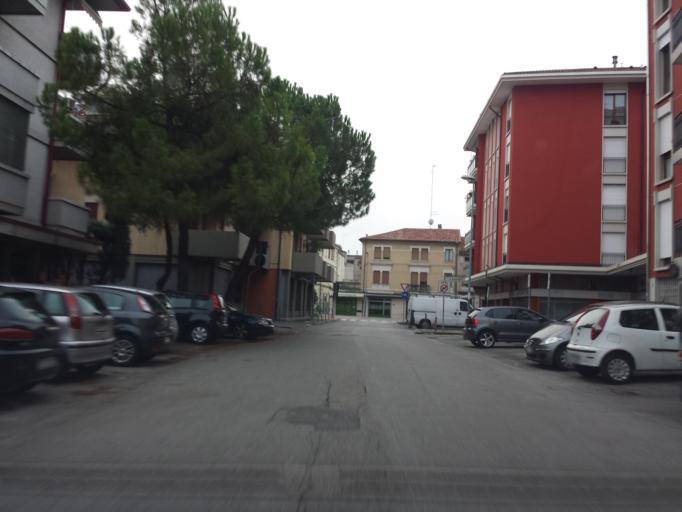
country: IT
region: Veneto
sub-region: Provincia di Padova
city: Padova
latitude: 45.4223
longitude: 11.8819
